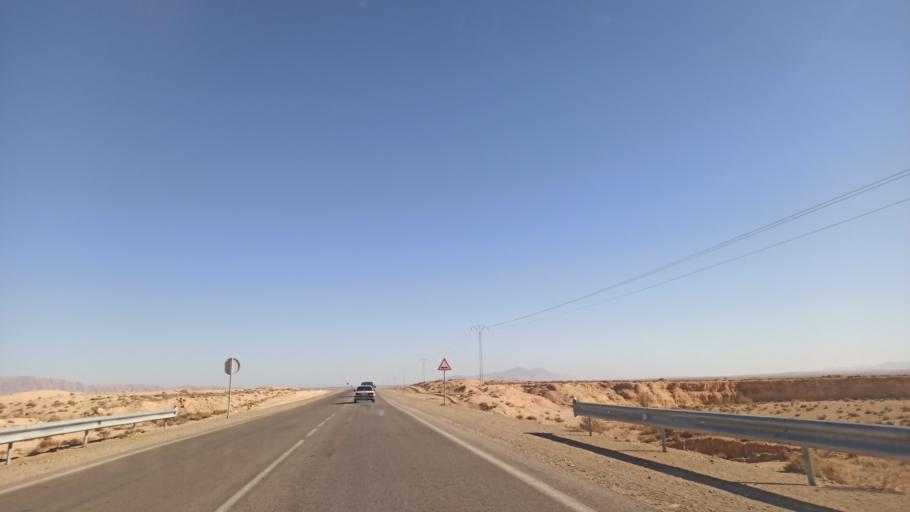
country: TN
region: Gafsa
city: Al Metlaoui
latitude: 34.3298
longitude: 8.5507
